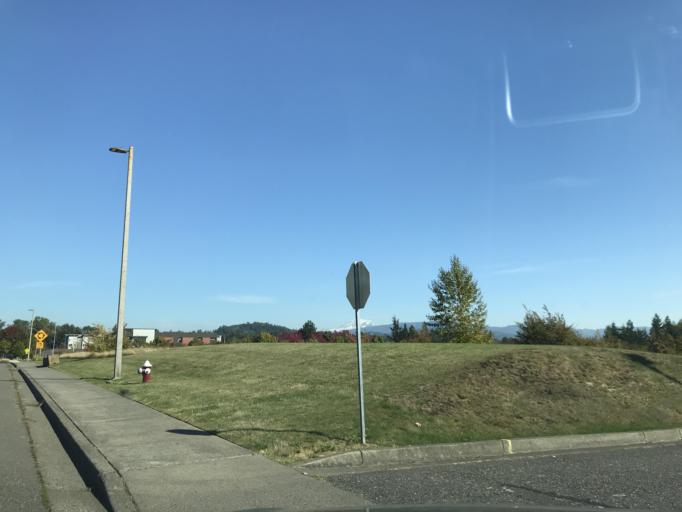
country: US
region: Washington
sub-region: Whatcom County
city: Bellingham
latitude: 48.7985
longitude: -122.4978
